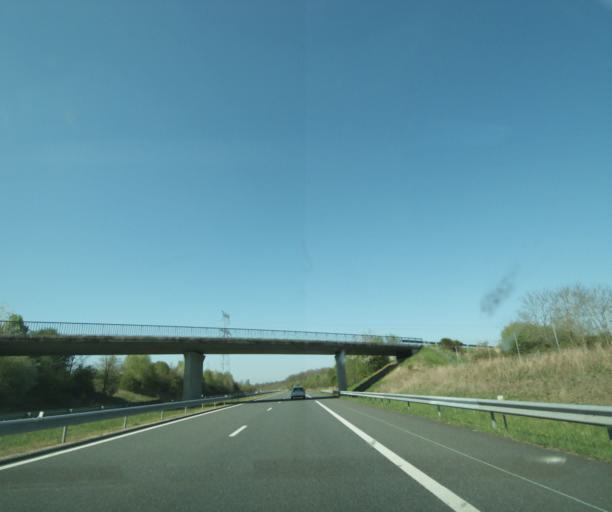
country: FR
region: Centre
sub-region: Departement du Loiret
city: Changy-les-Bois
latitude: 47.8121
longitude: 2.6949
